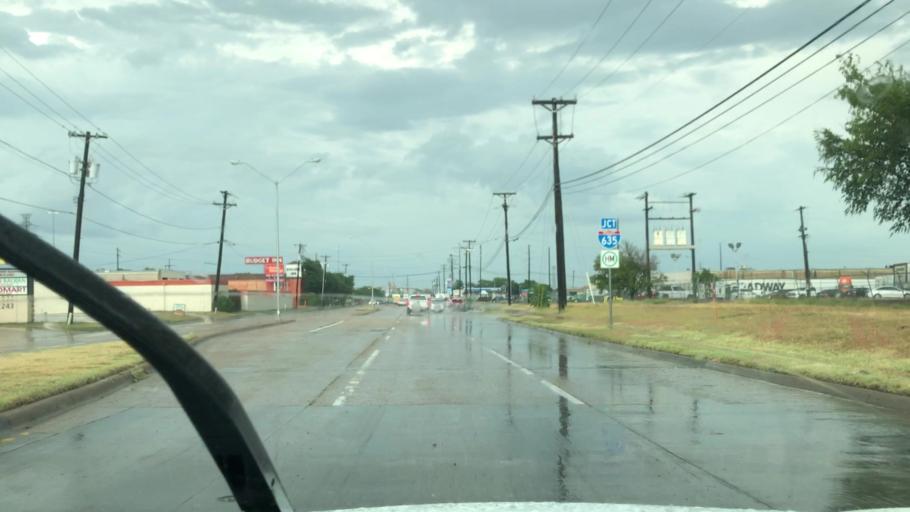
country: US
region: Texas
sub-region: Dallas County
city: Garland
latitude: 32.8641
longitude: -96.6693
